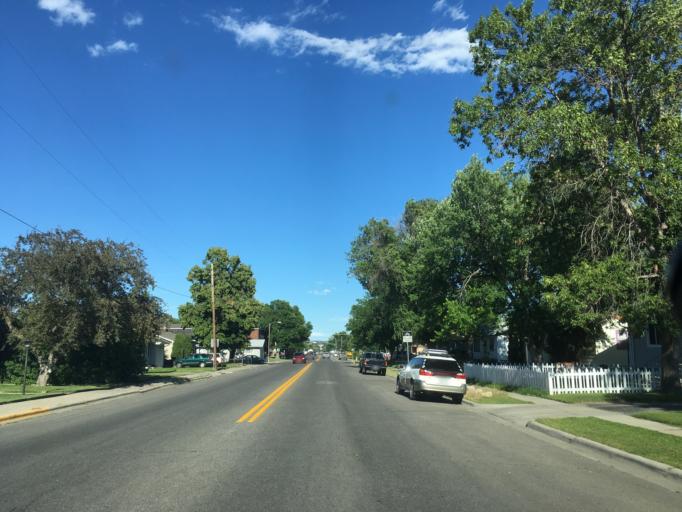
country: US
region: Montana
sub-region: Yellowstone County
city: Billings
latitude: 45.7806
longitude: -108.5606
